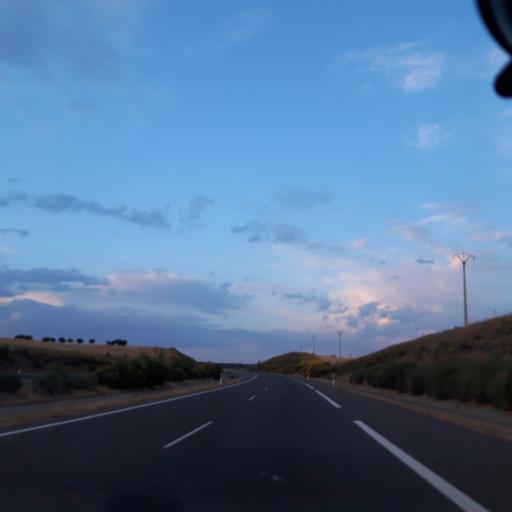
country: ES
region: Castille and Leon
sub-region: Provincia de Salamanca
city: Mozarbez
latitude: 40.8468
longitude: -5.6411
